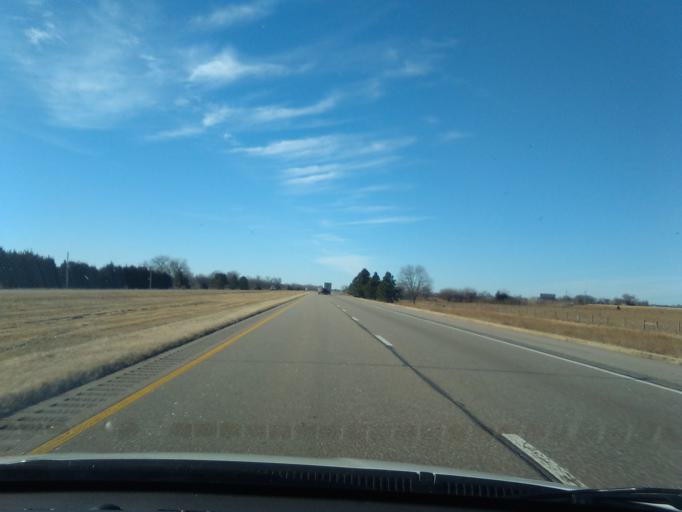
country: US
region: Nebraska
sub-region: Hall County
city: Grand Island
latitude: 40.8154
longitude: -98.4328
